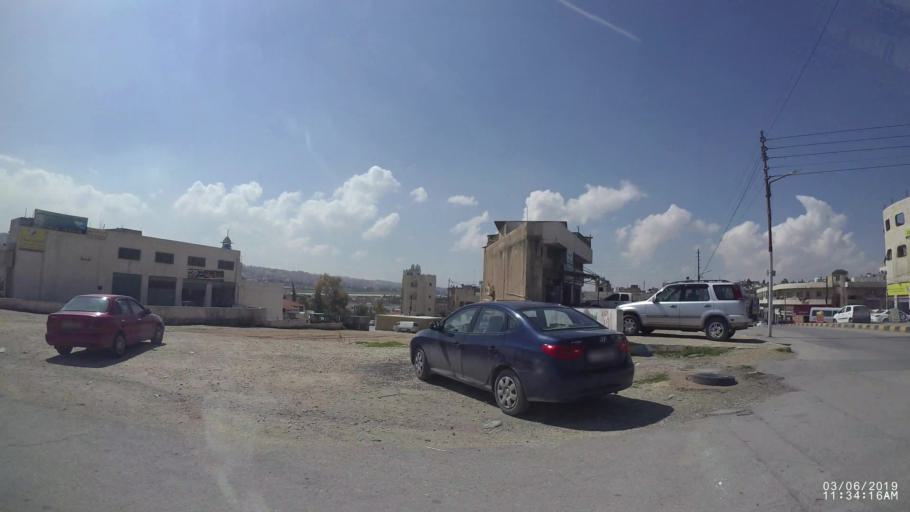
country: JO
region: Amman
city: Amman
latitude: 31.9807
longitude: 35.9980
